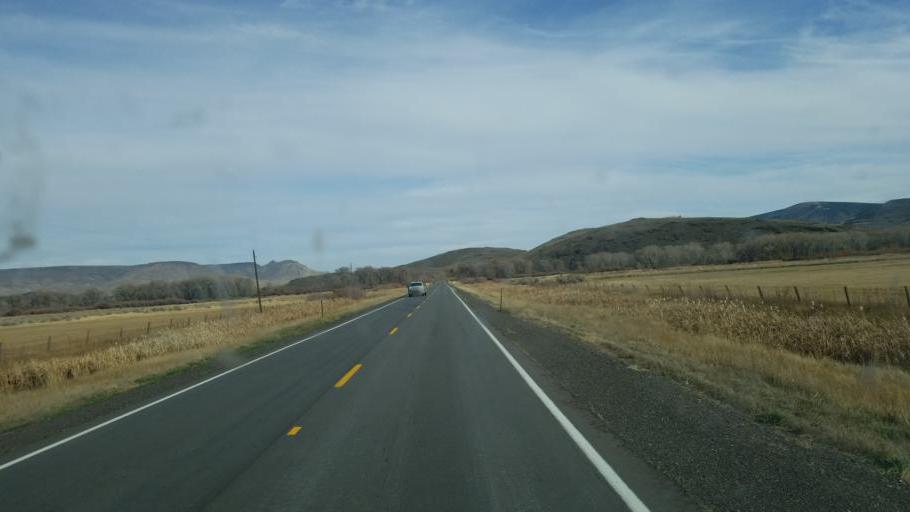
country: US
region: Colorado
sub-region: Conejos County
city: Conejos
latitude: 37.1738
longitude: -105.9053
